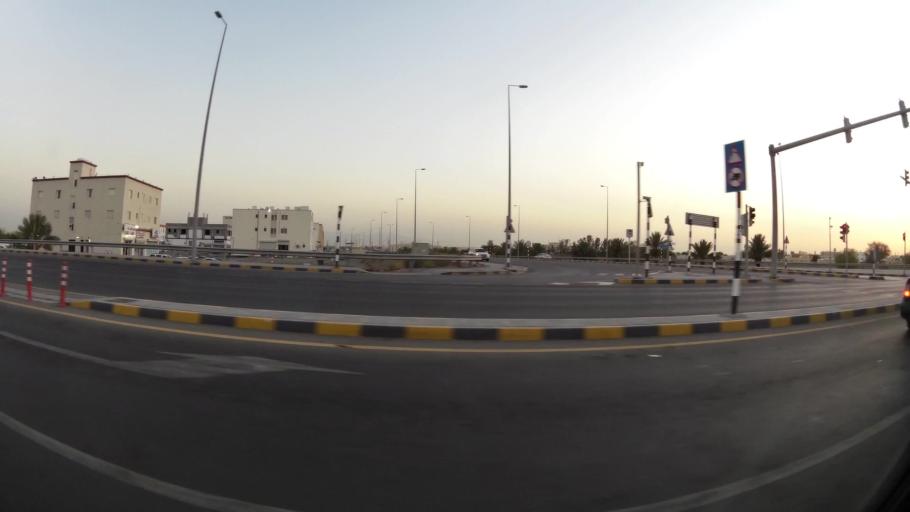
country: OM
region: Muhafazat Masqat
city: As Sib al Jadidah
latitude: 23.6664
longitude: 58.1938
